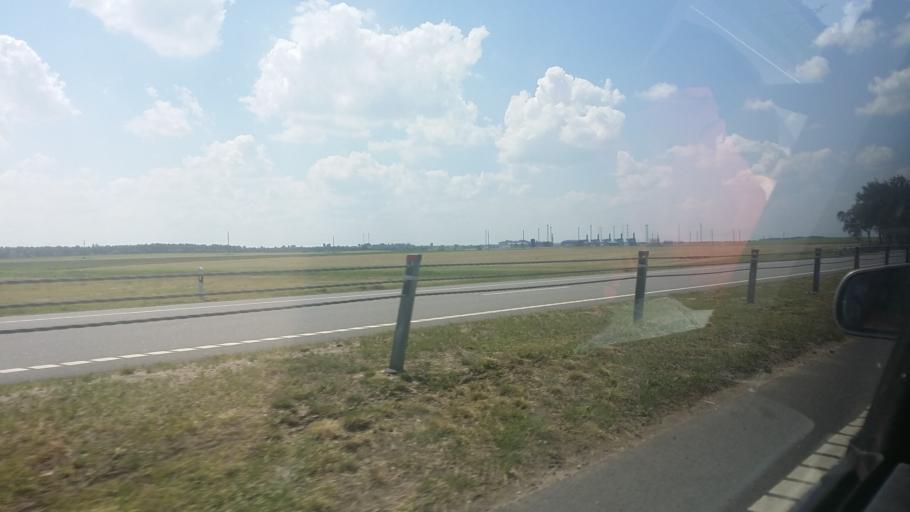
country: BY
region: Minsk
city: Luhavaya Slabada
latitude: 53.7615
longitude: 27.8907
